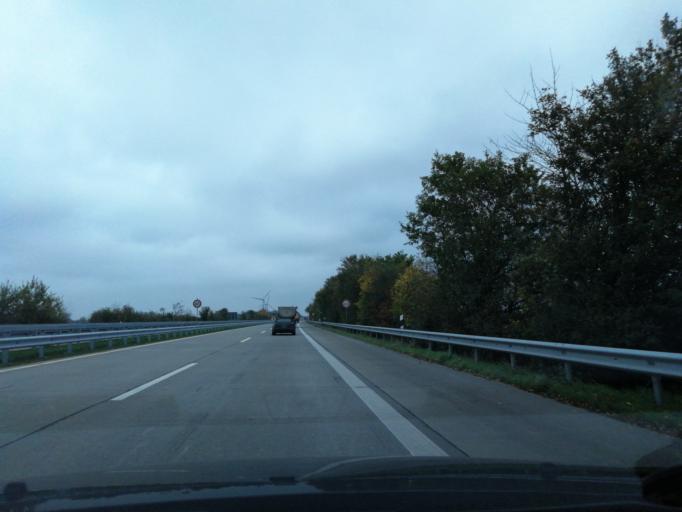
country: DE
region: Lower Saxony
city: Sande
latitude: 53.5347
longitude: 8.0207
